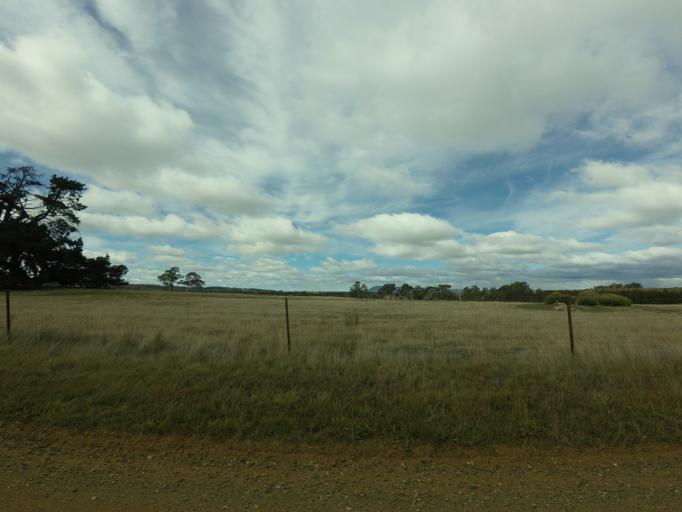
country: AU
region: Tasmania
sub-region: Brighton
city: Bridgewater
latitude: -42.4359
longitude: 147.3858
